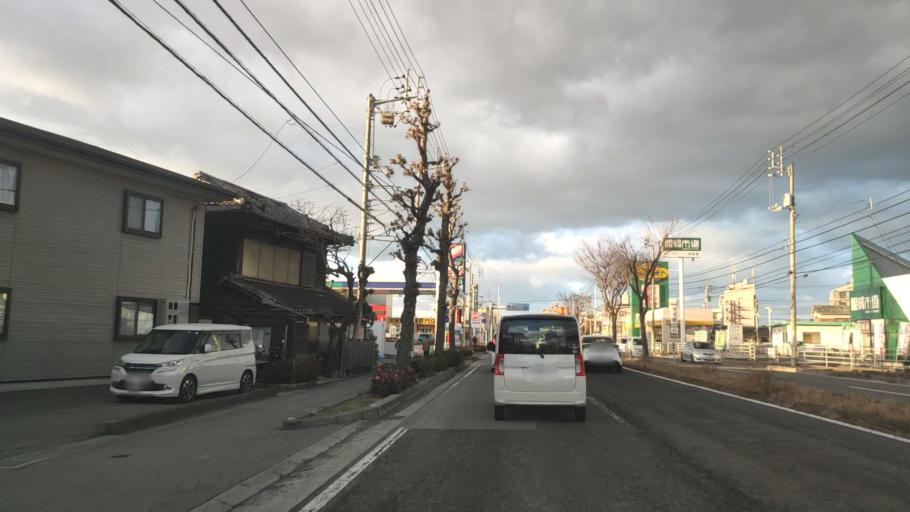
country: JP
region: Ehime
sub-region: Shikoku-chuo Shi
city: Matsuyama
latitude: 33.8079
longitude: 132.7807
